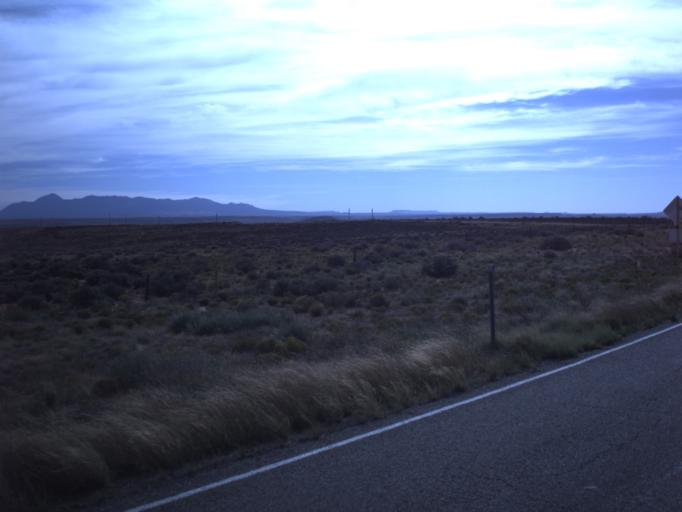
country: US
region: Utah
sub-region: San Juan County
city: Blanding
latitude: 37.3274
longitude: -109.3438
